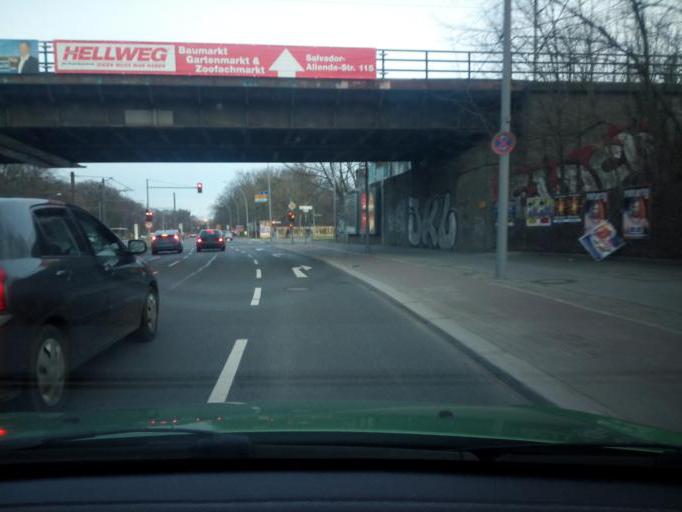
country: DE
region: Berlin
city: Kopenick Bezirk
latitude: 52.4555
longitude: 13.5571
